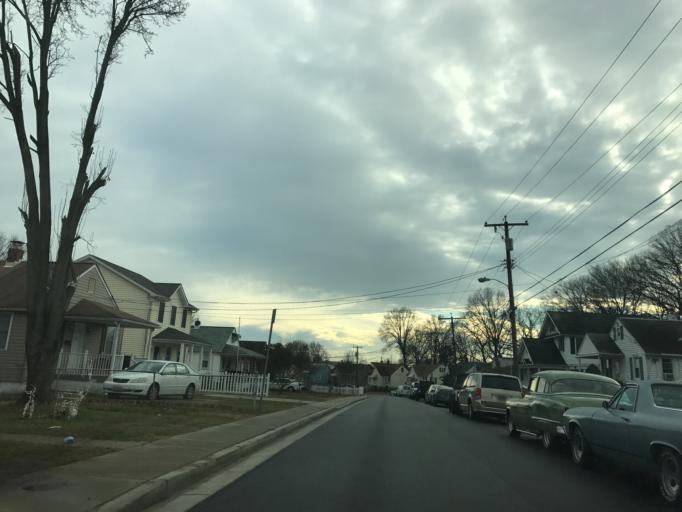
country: US
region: Maryland
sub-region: Baltimore County
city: Essex
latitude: 39.3144
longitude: -76.4725
